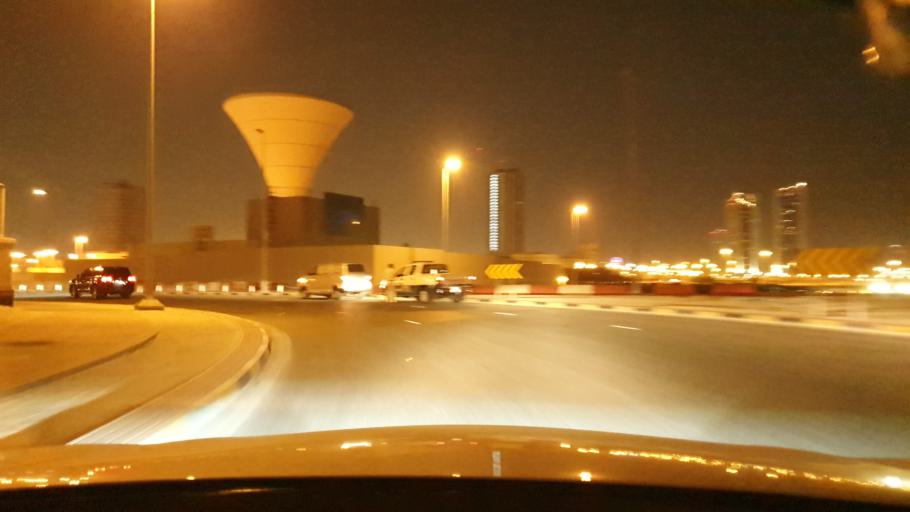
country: BH
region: Manama
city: Manama
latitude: 26.2379
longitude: 50.5708
